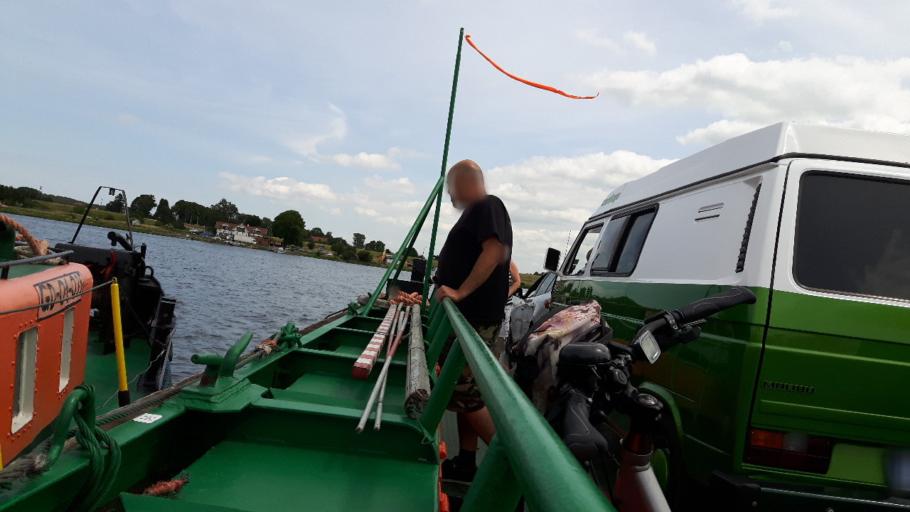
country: PL
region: Pomeranian Voivodeship
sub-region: Powiat nowodworski
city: Ostaszewo
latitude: 54.3331
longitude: 18.9387
